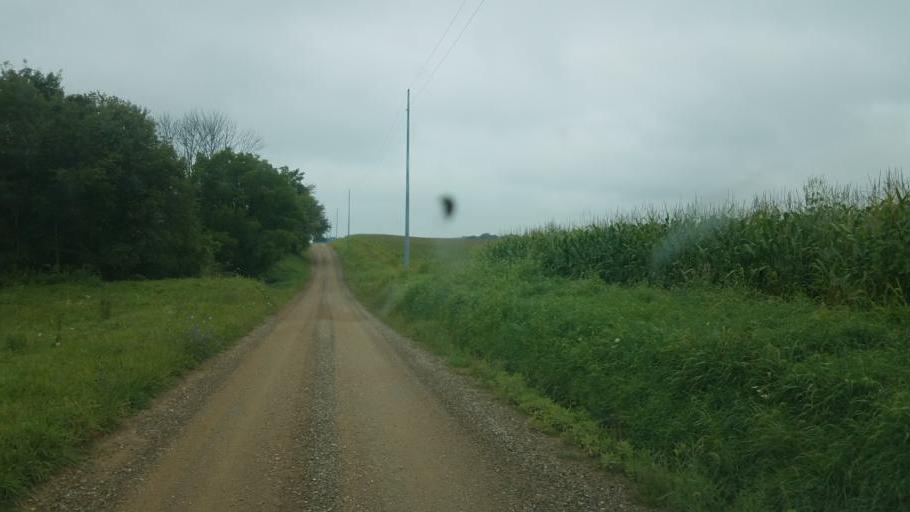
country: US
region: Ohio
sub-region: Licking County
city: Utica
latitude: 40.2709
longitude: -82.4114
